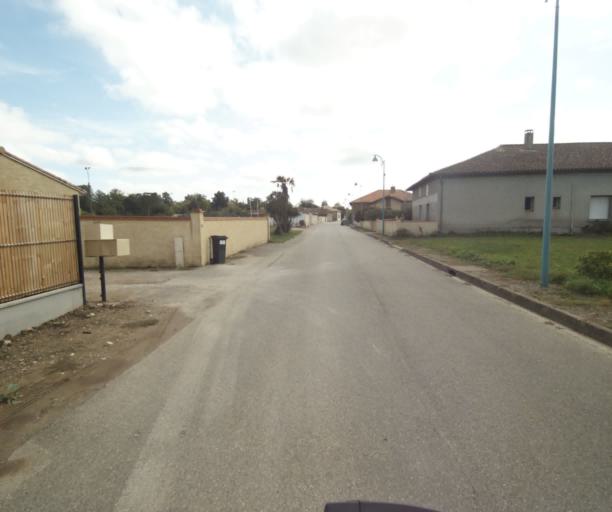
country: FR
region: Midi-Pyrenees
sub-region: Departement du Tarn-et-Garonne
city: Finhan
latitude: 43.9184
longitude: 1.2189
